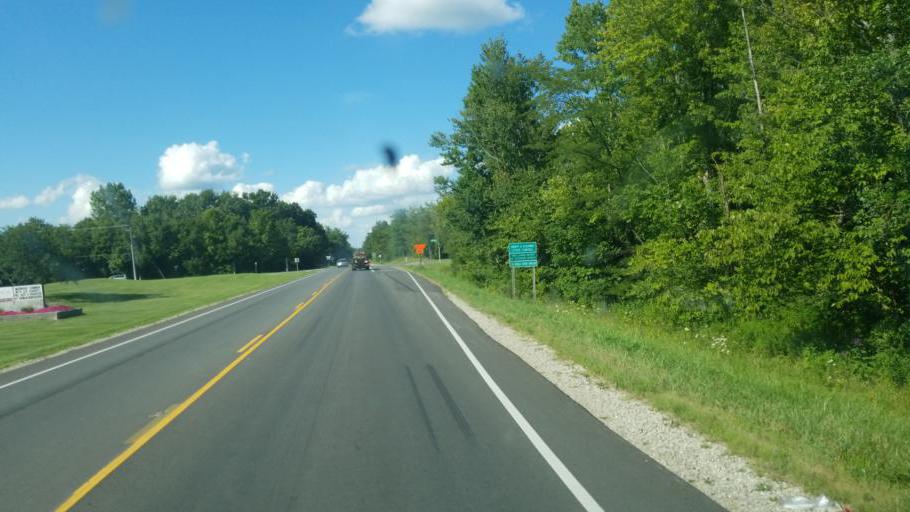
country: US
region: Ohio
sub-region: Delaware County
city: Sunbury
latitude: 40.1954
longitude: -82.9081
